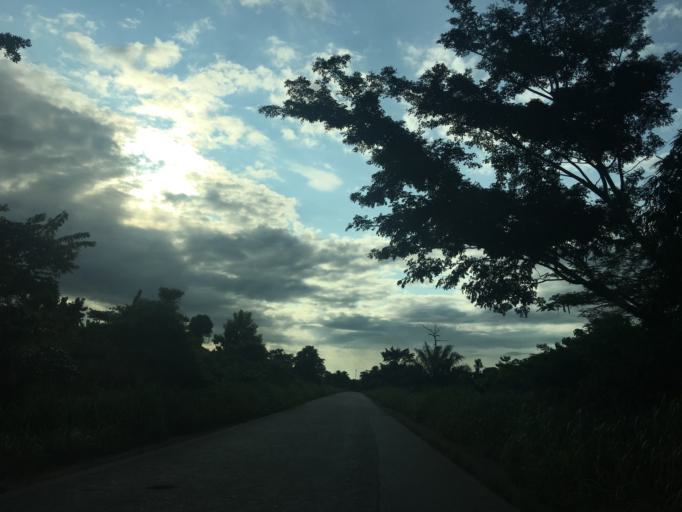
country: GH
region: Western
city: Bibiani
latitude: 6.2965
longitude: -2.2381
